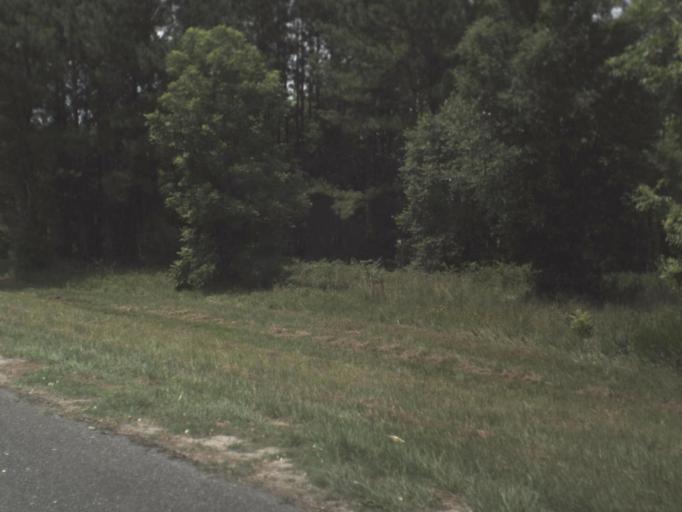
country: US
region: Florida
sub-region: Suwannee County
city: Live Oak
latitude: 30.1749
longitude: -82.9806
